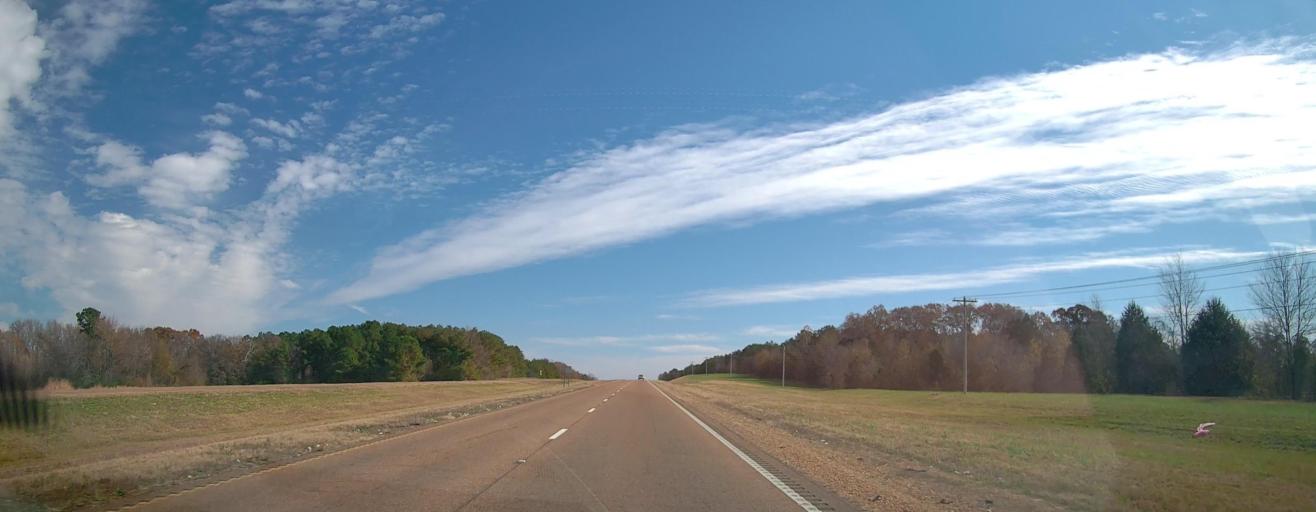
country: US
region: Tennessee
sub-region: Fayette County
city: Piperton
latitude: 34.9567
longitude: -89.5058
